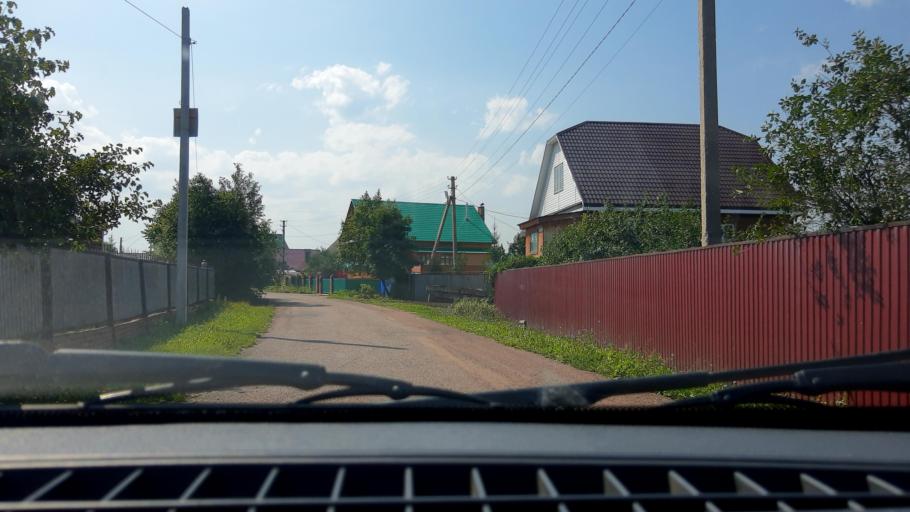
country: RU
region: Bashkortostan
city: Mikhaylovka
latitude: 54.8414
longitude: 55.8290
